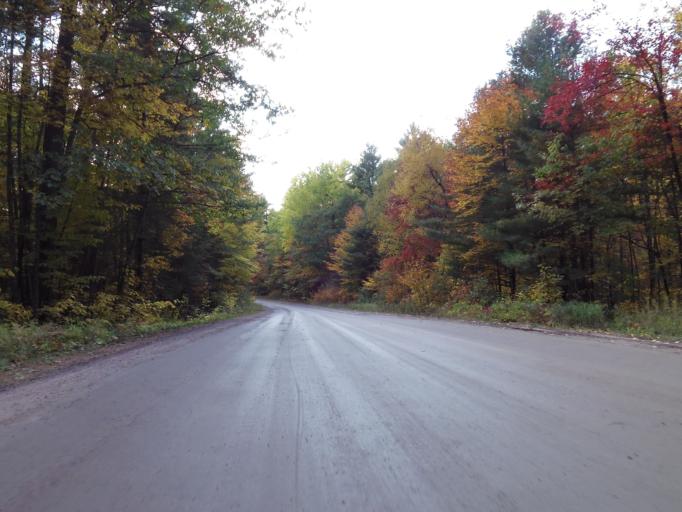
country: CA
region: Ontario
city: Deep River
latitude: 45.8935
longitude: -77.6190
